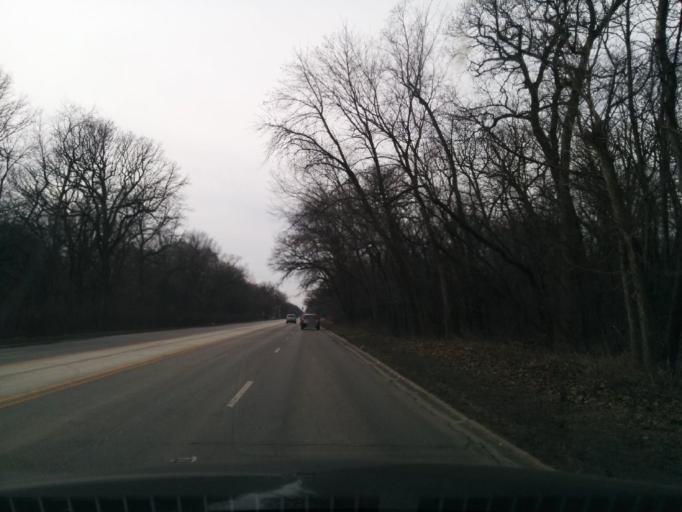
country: US
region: Illinois
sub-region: Cook County
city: La Grange Park
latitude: 41.8343
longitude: -87.8769
